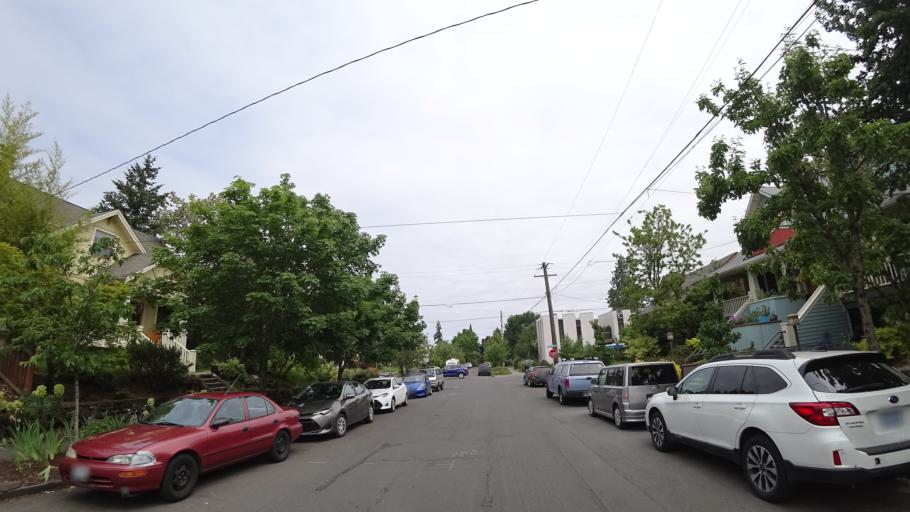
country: US
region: Oregon
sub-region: Multnomah County
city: Portland
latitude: 45.5623
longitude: -122.6338
